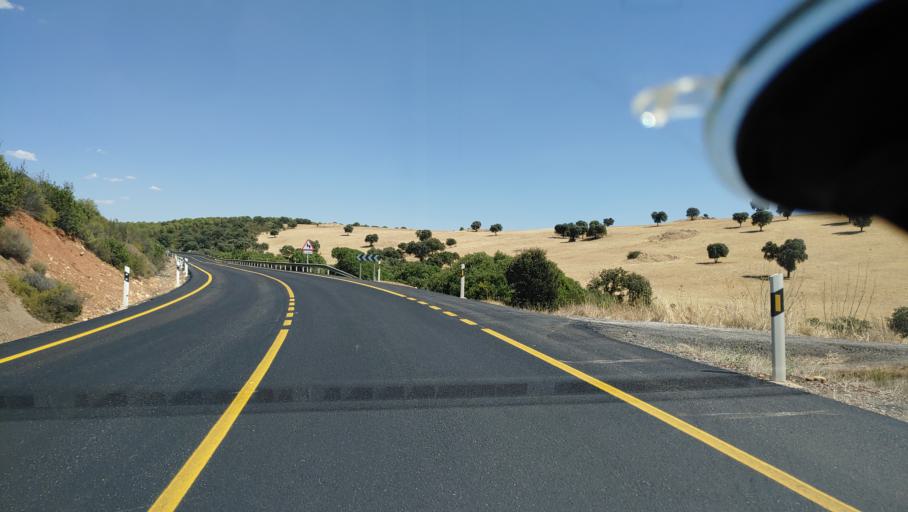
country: ES
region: Castille-La Mancha
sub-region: Provincia de Ciudad Real
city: Saceruela
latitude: 39.0136
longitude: -4.4627
